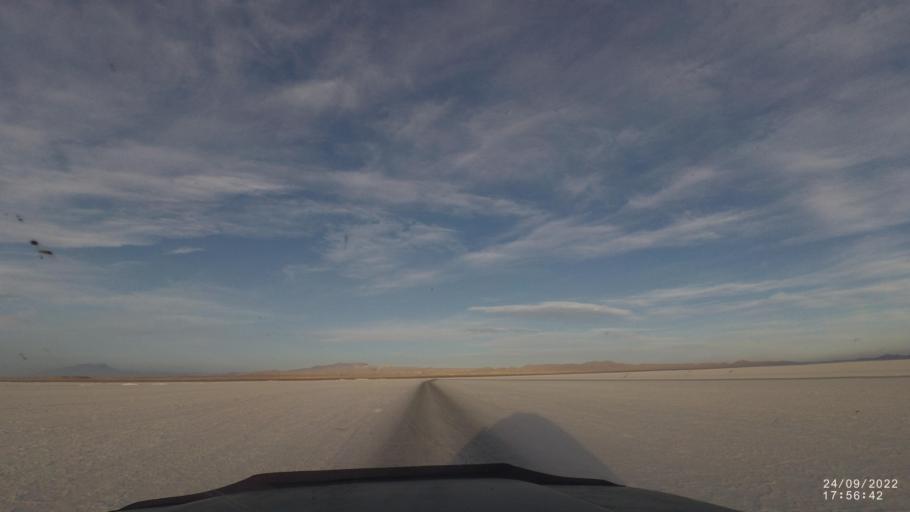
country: BO
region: Potosi
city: Colchani
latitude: -20.3232
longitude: -67.0073
